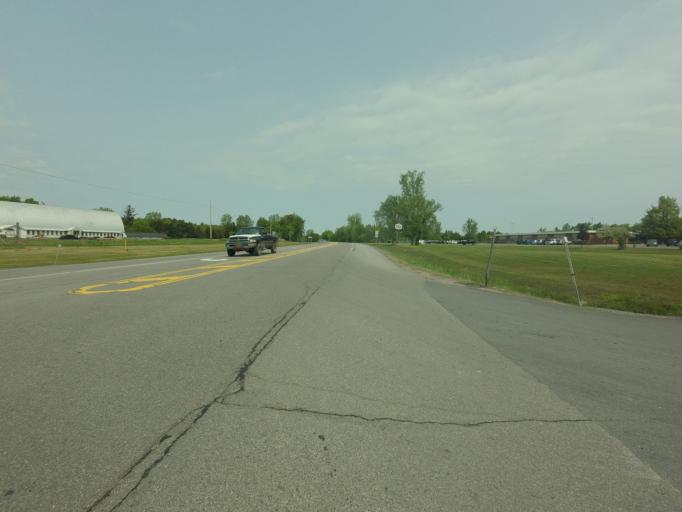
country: US
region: New York
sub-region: Jefferson County
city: Dexter
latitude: 44.0129
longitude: -76.0206
